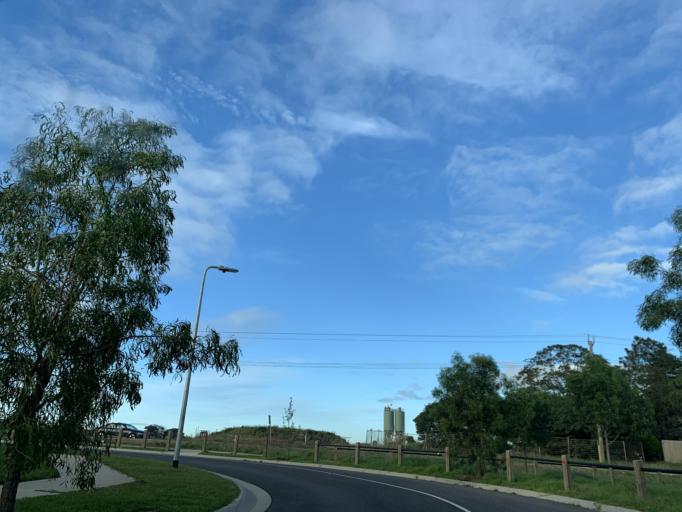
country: AU
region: Victoria
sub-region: Casey
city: Junction Village
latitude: -38.1326
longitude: 145.3209
